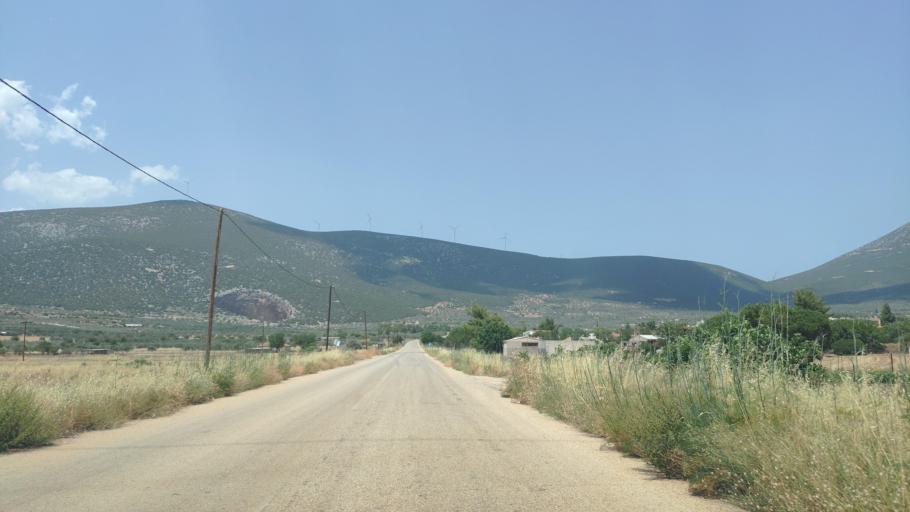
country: GR
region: Peloponnese
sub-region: Nomos Argolidos
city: Didyma
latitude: 37.4596
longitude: 23.1685
